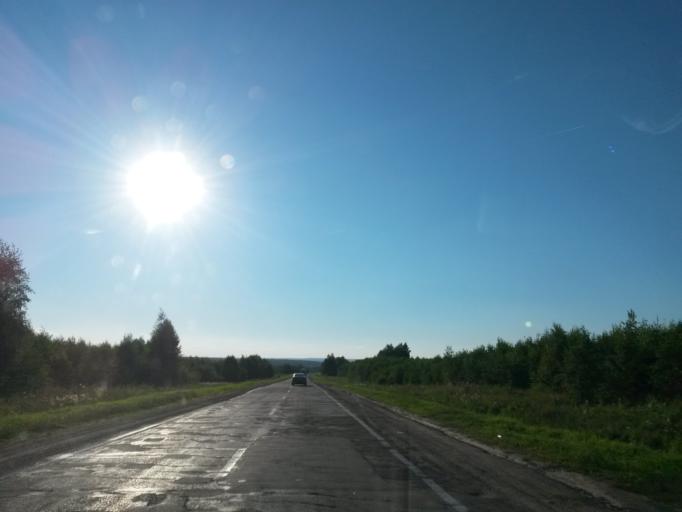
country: RU
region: Jaroslavl
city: Gavrilov-Yam
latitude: 57.2734
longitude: 39.9441
